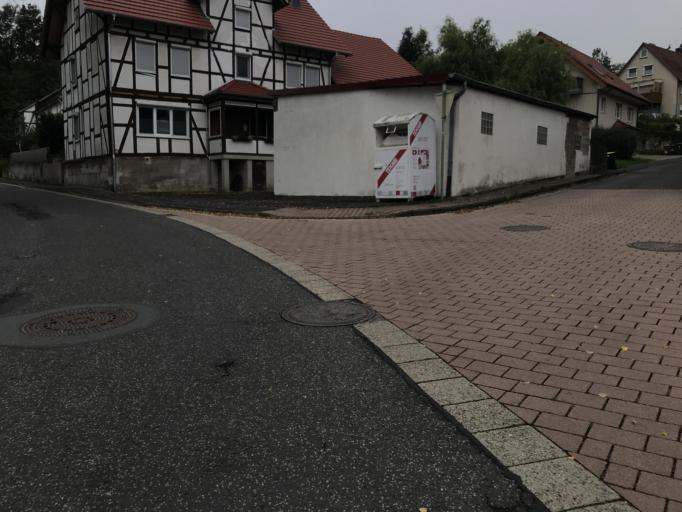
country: DE
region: Hesse
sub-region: Regierungsbezirk Kassel
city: Fuldabruck
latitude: 51.2336
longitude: 9.4669
